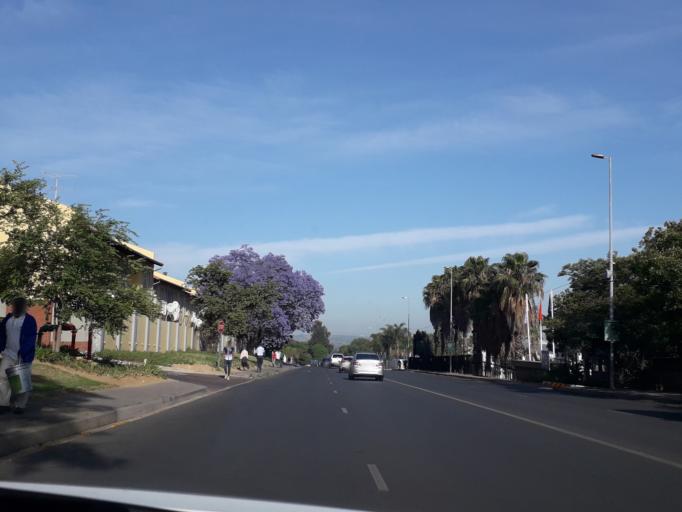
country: ZA
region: Gauteng
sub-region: City of Johannesburg Metropolitan Municipality
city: Johannesburg
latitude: -26.0893
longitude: 28.0006
